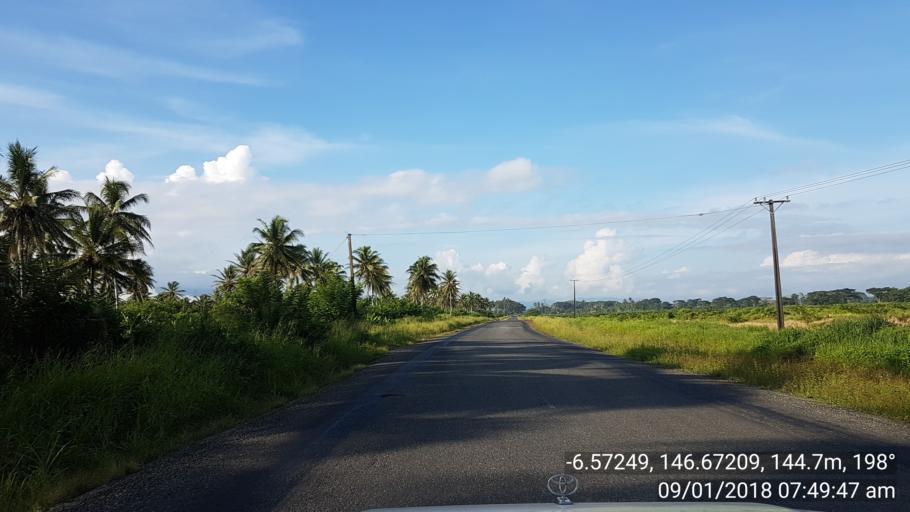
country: PG
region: Morobe
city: Lae
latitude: -6.5721
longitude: 146.6724
